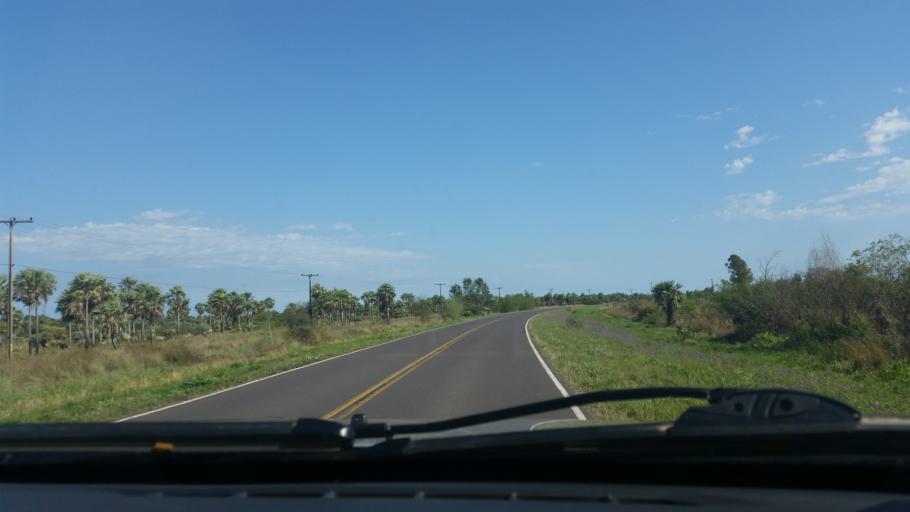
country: PY
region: Presidente Hayes
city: Benjamin Aceval
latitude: -24.7046
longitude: -57.9621
